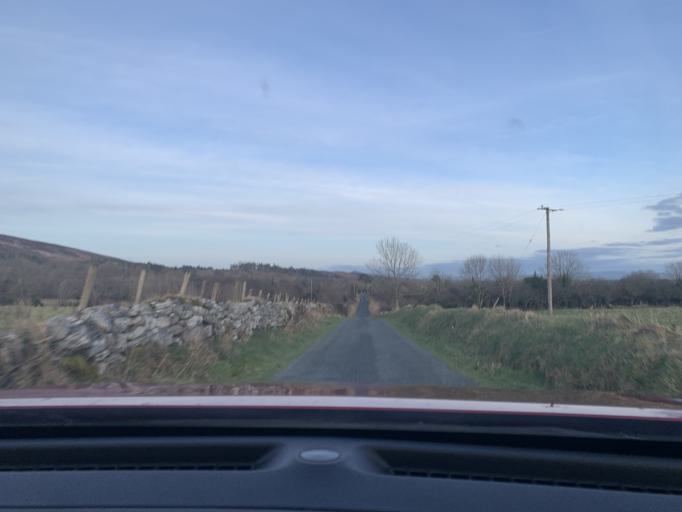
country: IE
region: Connaught
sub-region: Sligo
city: Strandhill
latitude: 54.1777
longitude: -8.6226
